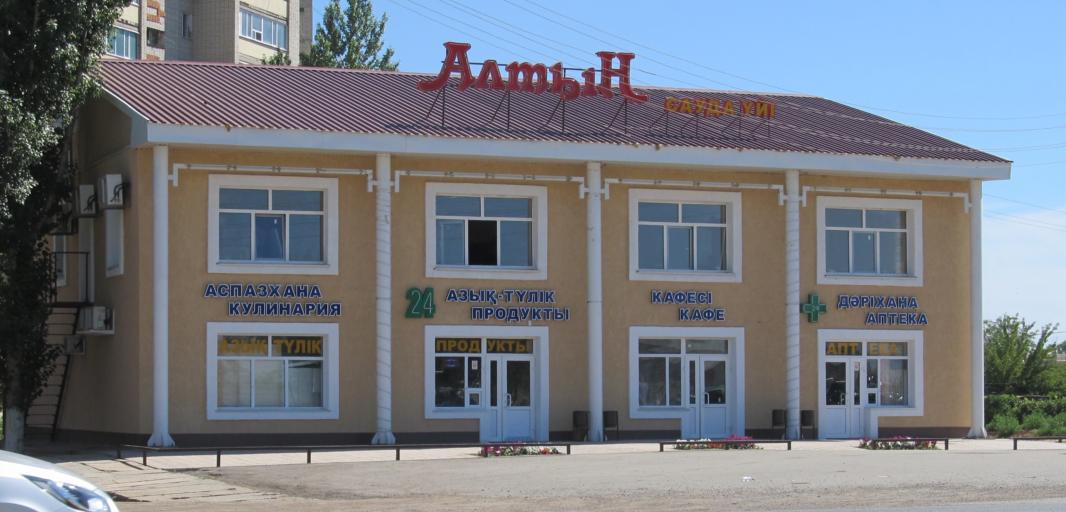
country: KZ
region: Batys Qazaqstan
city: Oral
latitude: 51.2502
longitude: 51.4132
